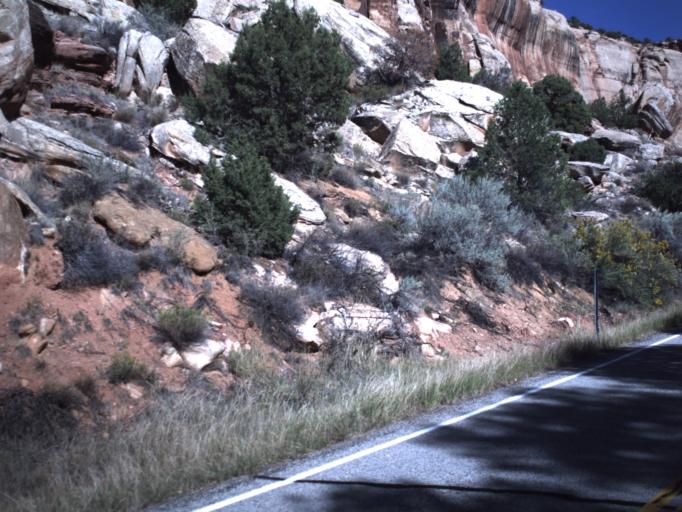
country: US
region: Utah
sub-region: San Juan County
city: Monticello
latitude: 38.0211
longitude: -109.5402
